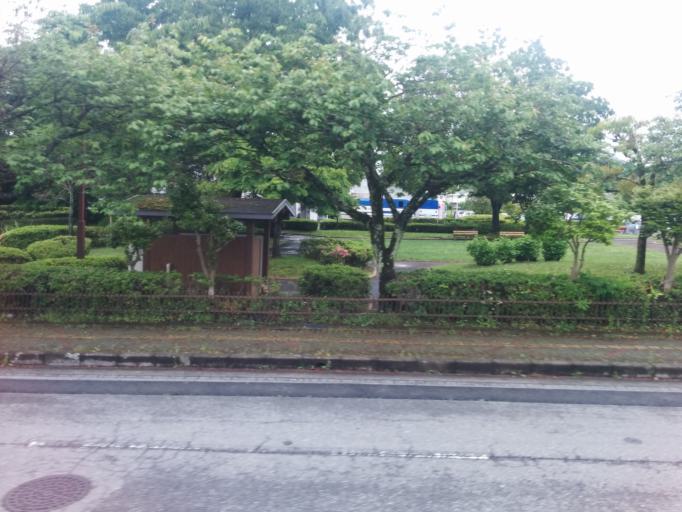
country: JP
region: Tochigi
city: Imaichi
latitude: 36.7218
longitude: 139.6847
